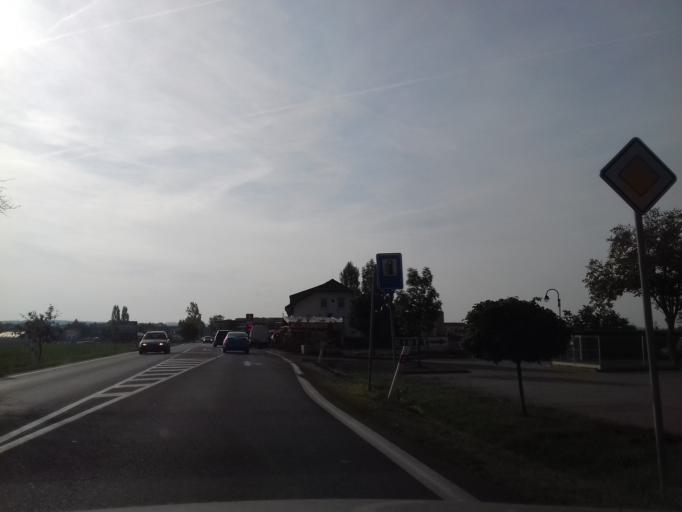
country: CZ
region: Central Bohemia
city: Vestec
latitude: 49.9744
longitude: 14.5019
